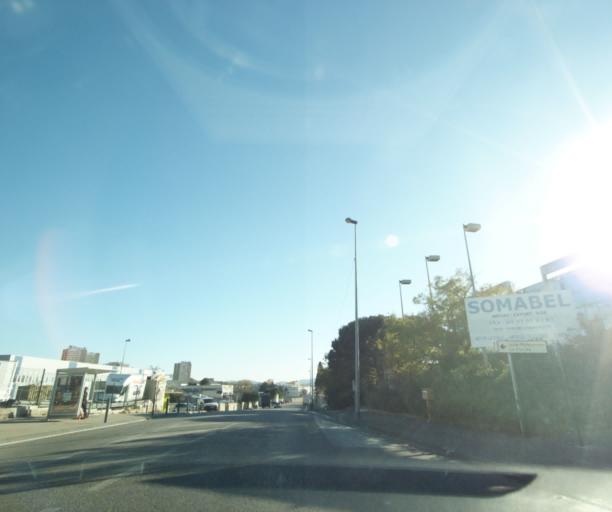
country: FR
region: Provence-Alpes-Cote d'Azur
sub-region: Departement des Bouches-du-Rhone
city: Marseille 14
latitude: 43.3367
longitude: 5.3742
